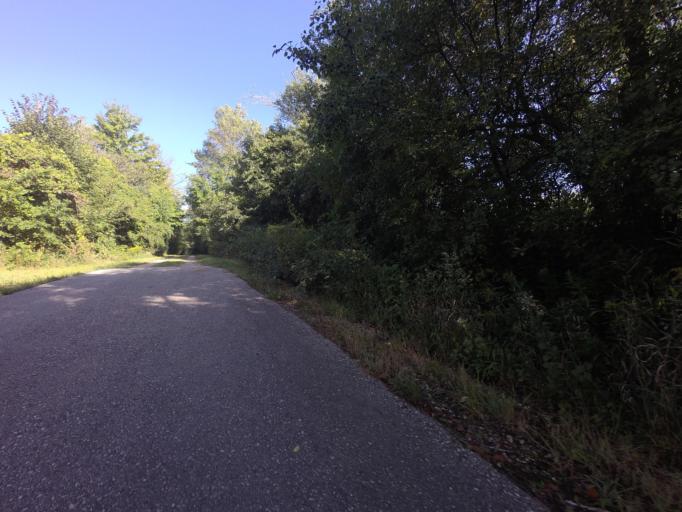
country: CA
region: Ontario
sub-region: Wellington County
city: Guelph
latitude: 43.6532
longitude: -80.4193
